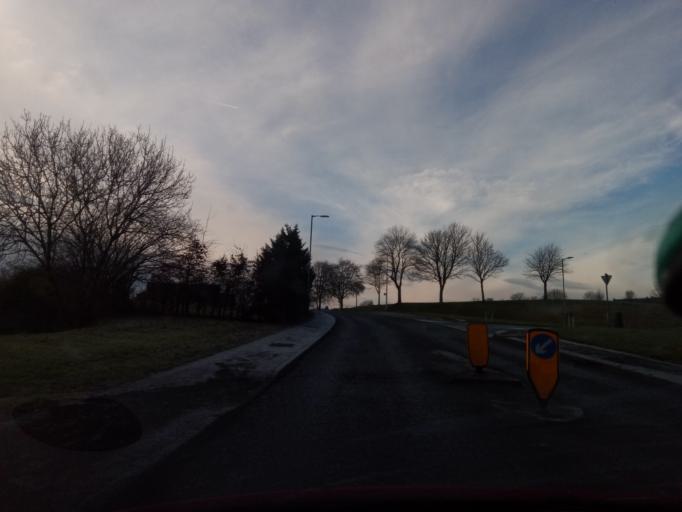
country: GB
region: Scotland
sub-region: The Scottish Borders
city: Hawick
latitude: 55.4383
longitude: -2.7598
